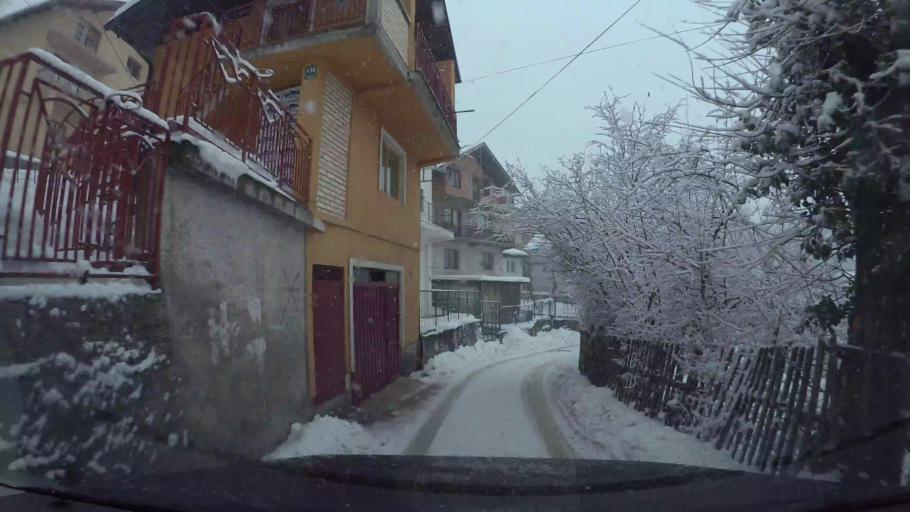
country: BA
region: Federation of Bosnia and Herzegovina
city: Kobilja Glava
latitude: 43.8494
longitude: 18.4558
